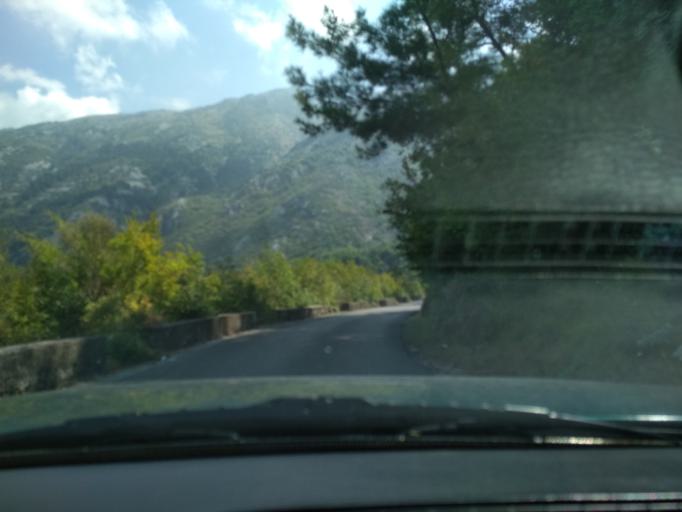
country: ME
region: Kotor
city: Kotor
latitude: 42.3997
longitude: 18.7619
